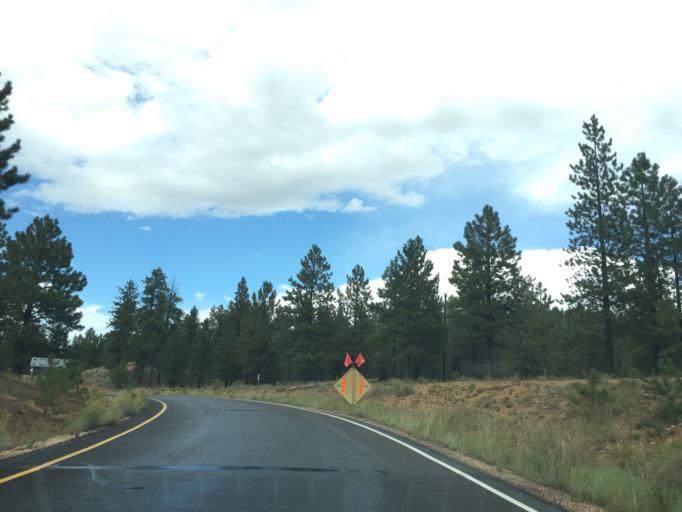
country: US
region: Utah
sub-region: Garfield County
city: Panguitch
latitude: 37.6401
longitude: -112.1688
